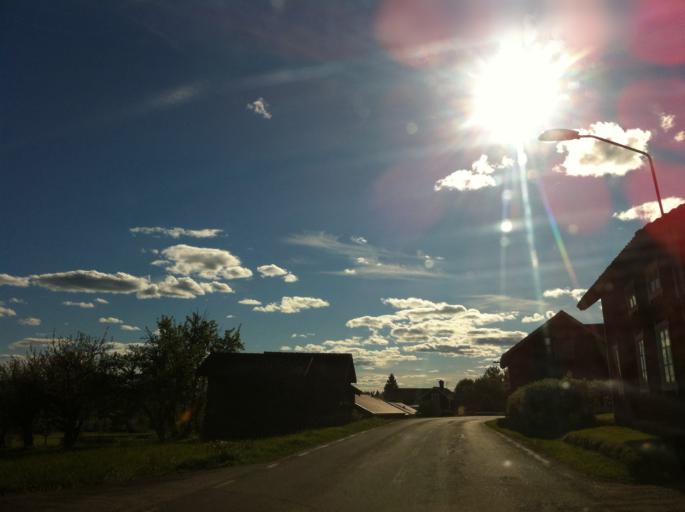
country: SE
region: Dalarna
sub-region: Leksand Municipality
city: Siljansnas
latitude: 60.7707
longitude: 14.8672
